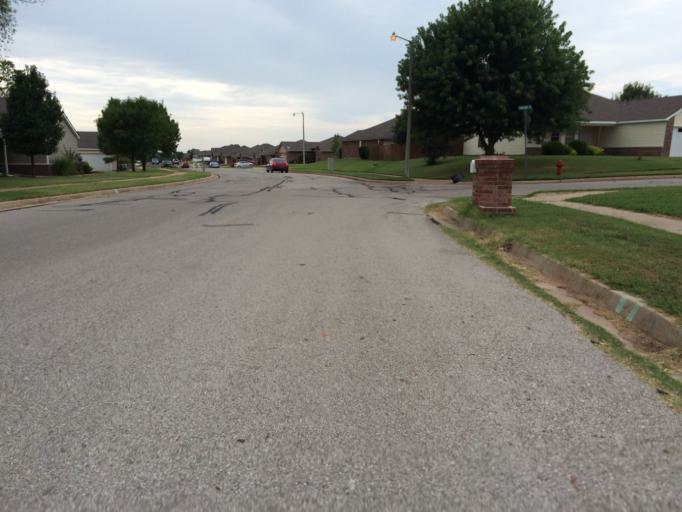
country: US
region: Oklahoma
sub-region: Cleveland County
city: Hall Park
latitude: 35.2549
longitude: -97.4268
